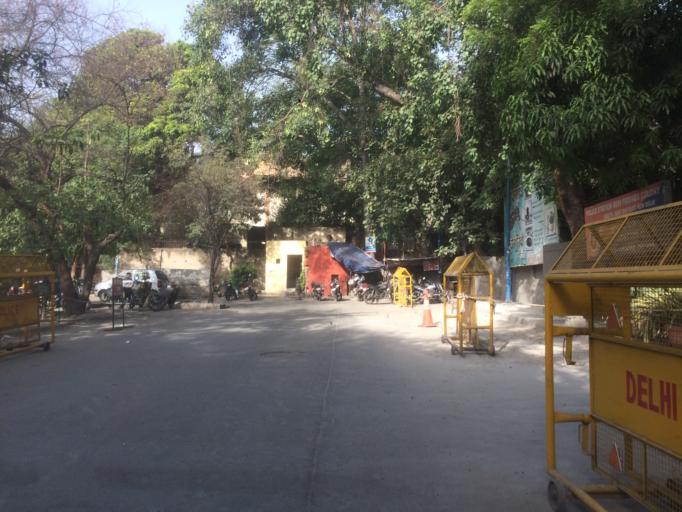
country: IN
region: Uttar Pradesh
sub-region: Gautam Buddha Nagar
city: Noida
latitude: 28.5622
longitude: 77.2677
